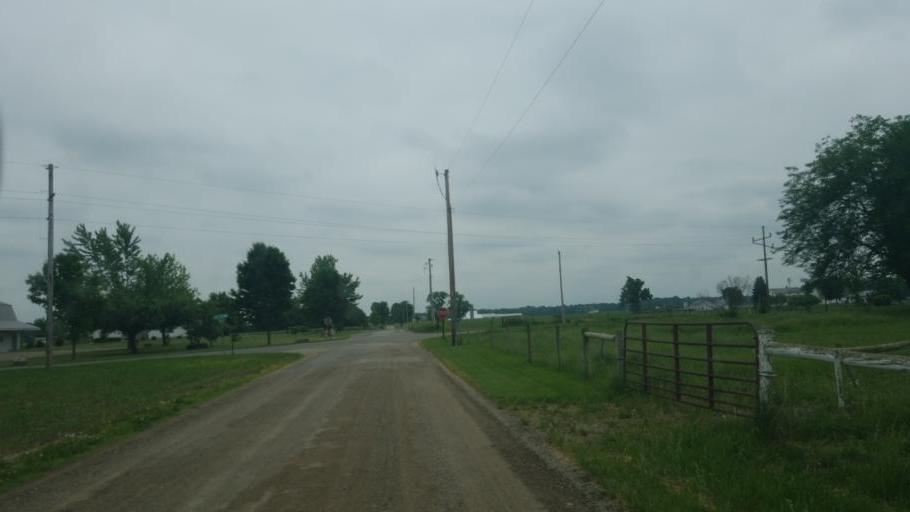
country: US
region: Indiana
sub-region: Elkhart County
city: Nappanee
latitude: 41.4744
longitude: -86.0595
